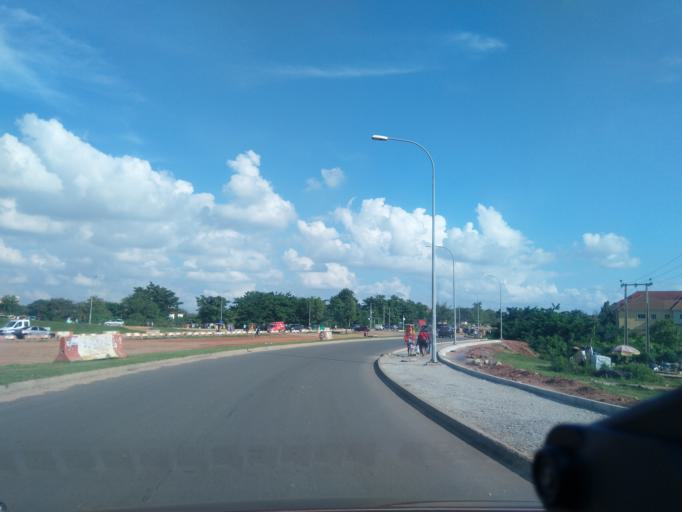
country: NG
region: Abuja Federal Capital Territory
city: Abuja
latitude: 9.0649
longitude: 7.4098
